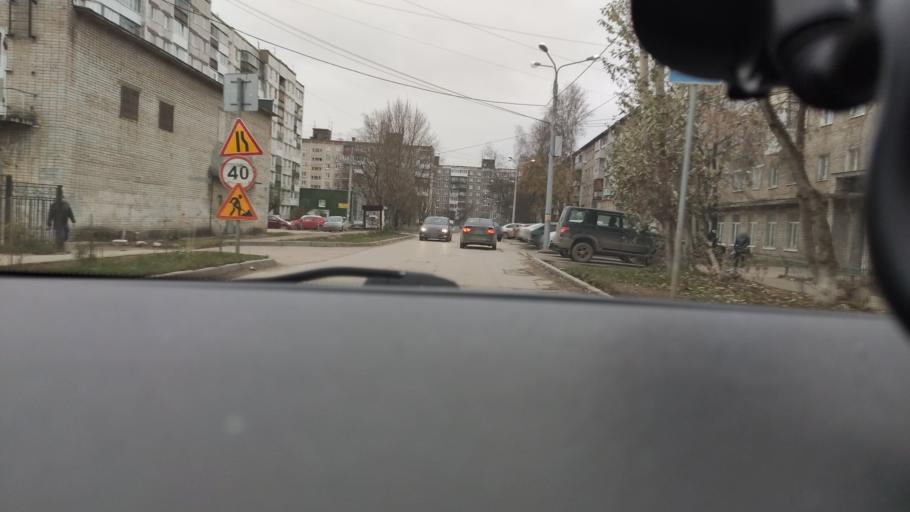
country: RU
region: Perm
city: Perm
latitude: 57.9654
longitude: 56.2326
